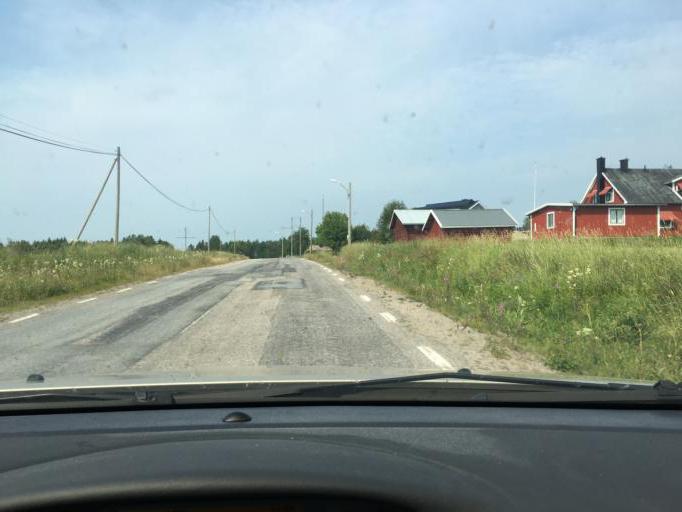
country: SE
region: Norrbotten
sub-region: Kalix Kommun
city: Rolfs
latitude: 65.7731
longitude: 23.0088
